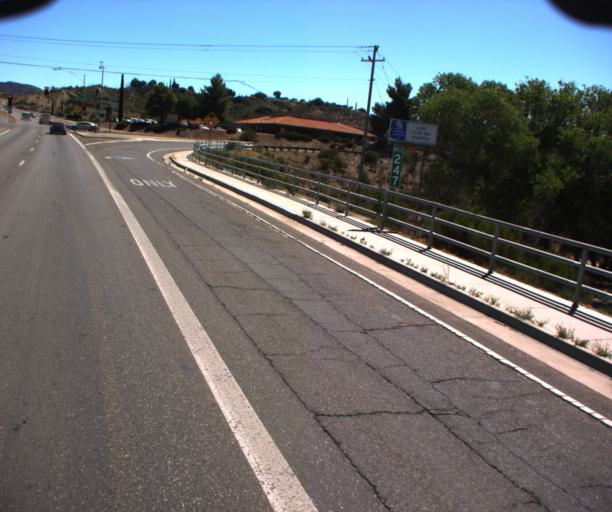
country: US
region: Arizona
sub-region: Gila County
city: Claypool
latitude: 33.4158
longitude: -110.8294
